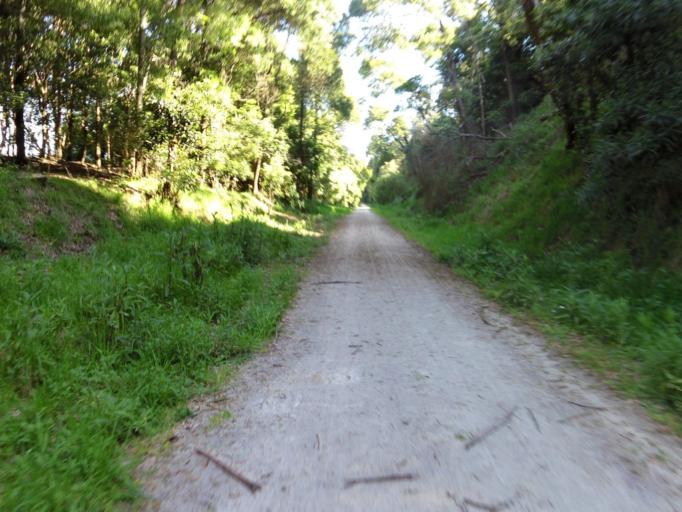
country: AU
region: Victoria
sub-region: Latrobe
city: Morwell
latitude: -38.6761
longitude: 146.1622
